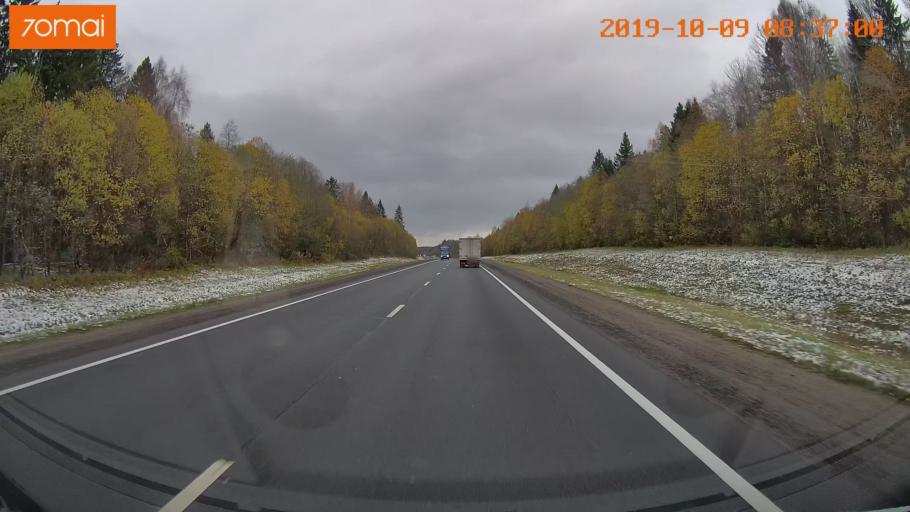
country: RU
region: Vologda
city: Gryazovets
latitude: 58.9347
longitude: 40.1756
